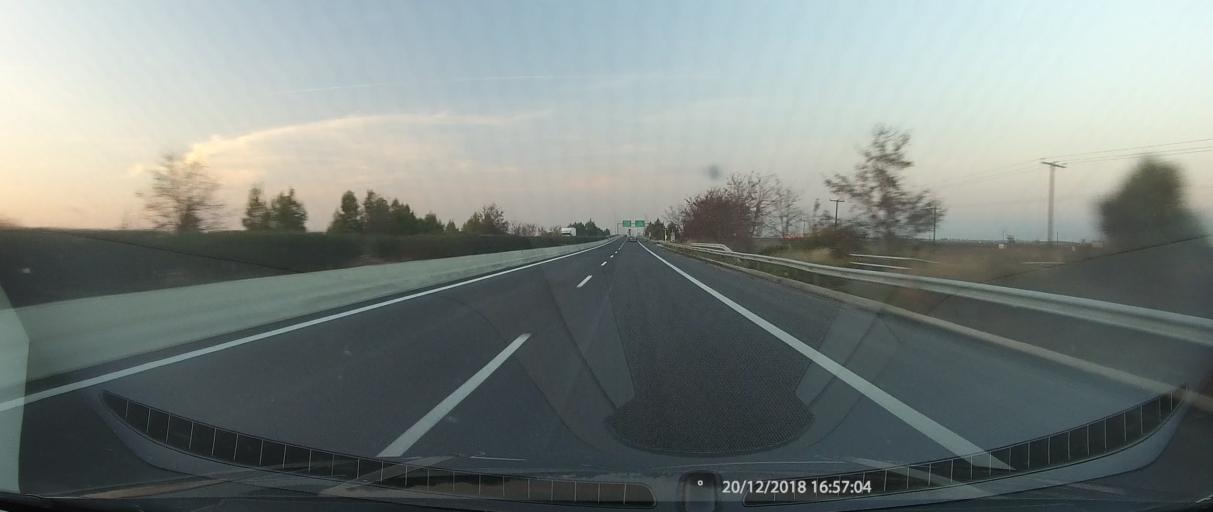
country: GR
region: Thessaly
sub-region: Nomos Larisis
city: Nikaia
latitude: 39.5676
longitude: 22.4867
